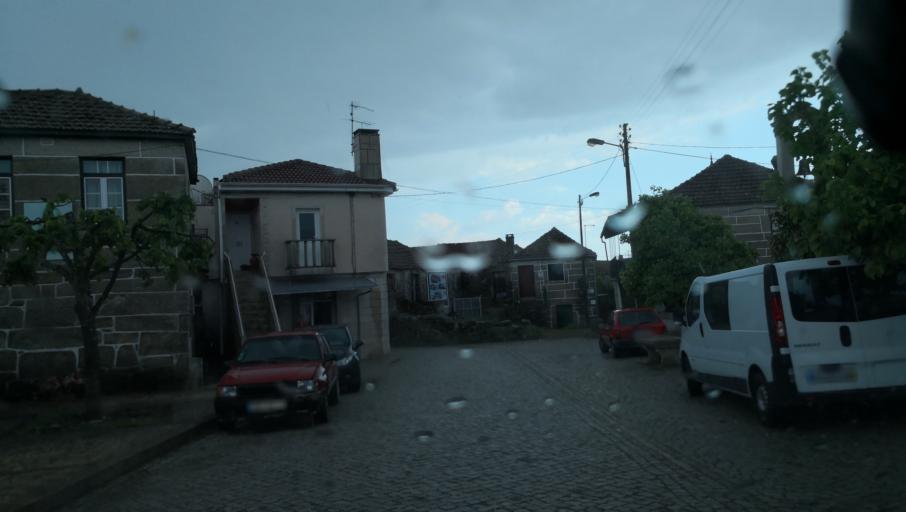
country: PT
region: Vila Real
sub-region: Vila Real
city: Vila Real
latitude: 41.3575
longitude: -7.6988
